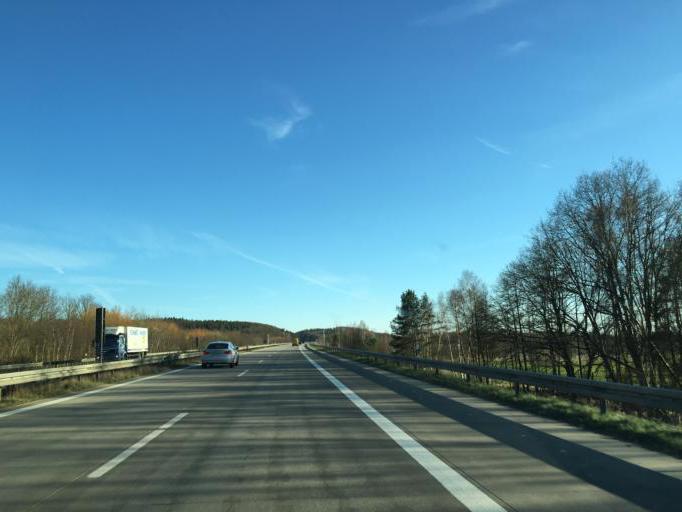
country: DE
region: Mecklenburg-Vorpommern
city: Lalendorf
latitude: 53.7676
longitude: 12.3237
